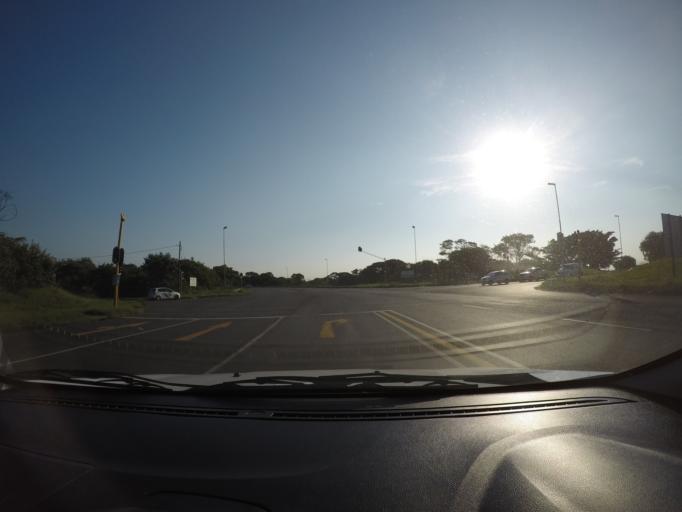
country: ZA
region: KwaZulu-Natal
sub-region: uThungulu District Municipality
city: Richards Bay
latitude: -28.7679
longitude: 32.0153
